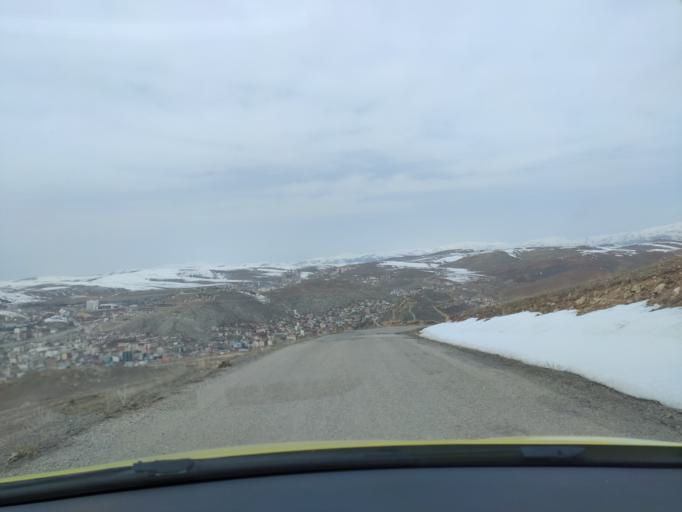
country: TR
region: Bayburt
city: Bayburt
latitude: 40.2578
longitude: 40.2406
